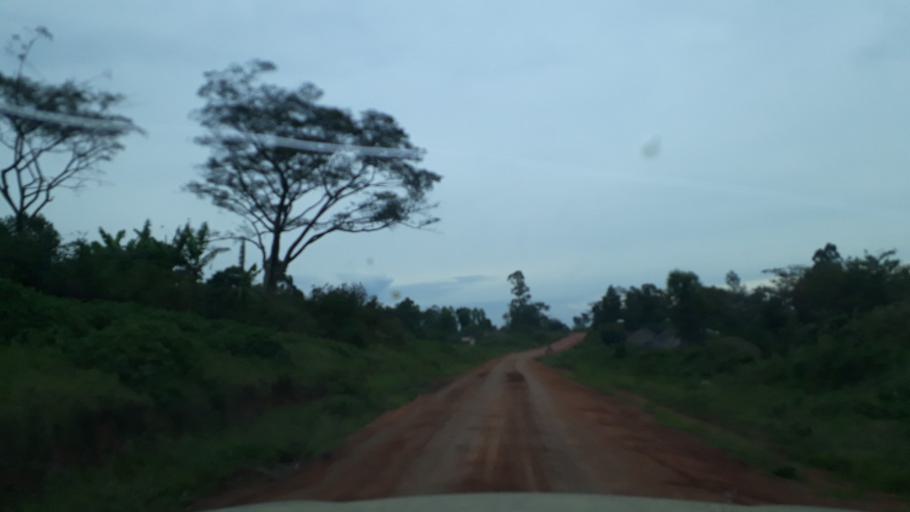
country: UG
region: Northern Region
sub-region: Zombo District
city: Paidha
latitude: 2.1850
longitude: 30.7252
